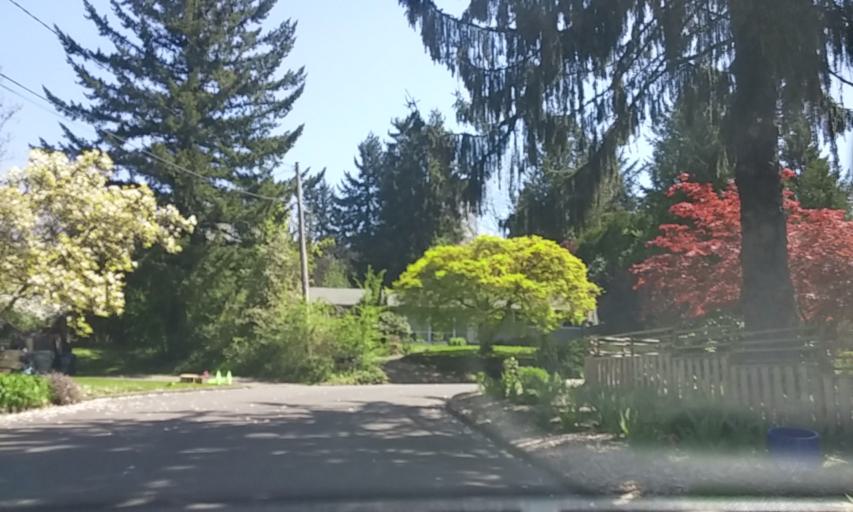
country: US
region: Oregon
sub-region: Washington County
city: West Haven
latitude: 45.5201
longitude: -122.7711
